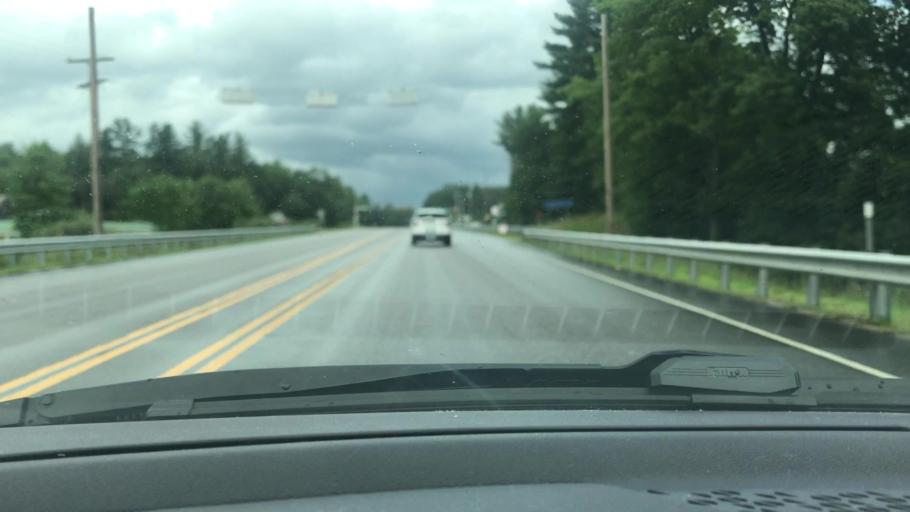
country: US
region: New Hampshire
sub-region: Merrimack County
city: Chichester
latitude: 43.2516
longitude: -71.4603
